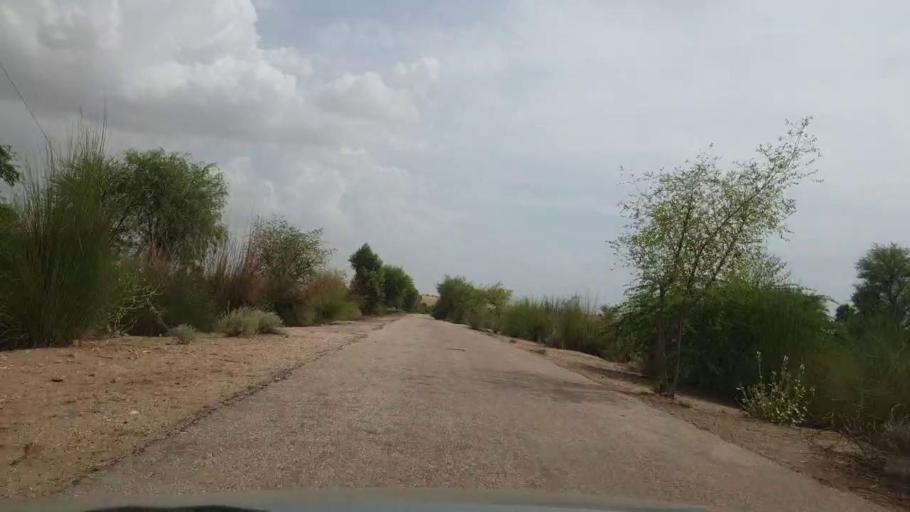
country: PK
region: Sindh
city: Bozdar
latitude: 27.0818
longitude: 69.0136
